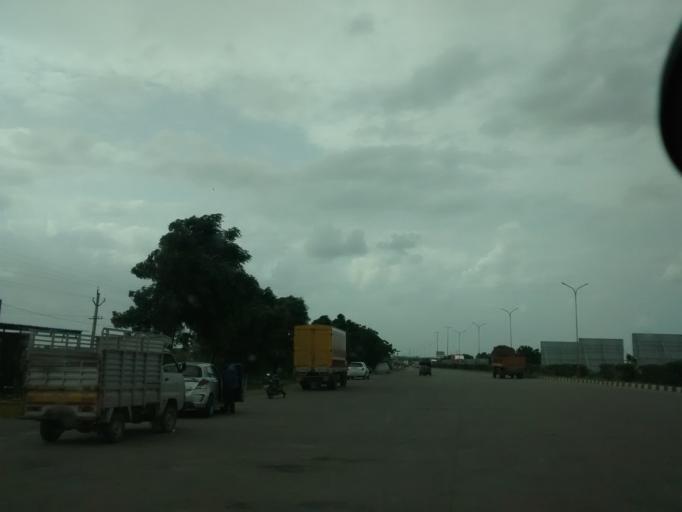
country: IN
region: Telangana
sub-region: Mahbubnagar
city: Alampur
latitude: 15.8886
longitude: 78.0169
